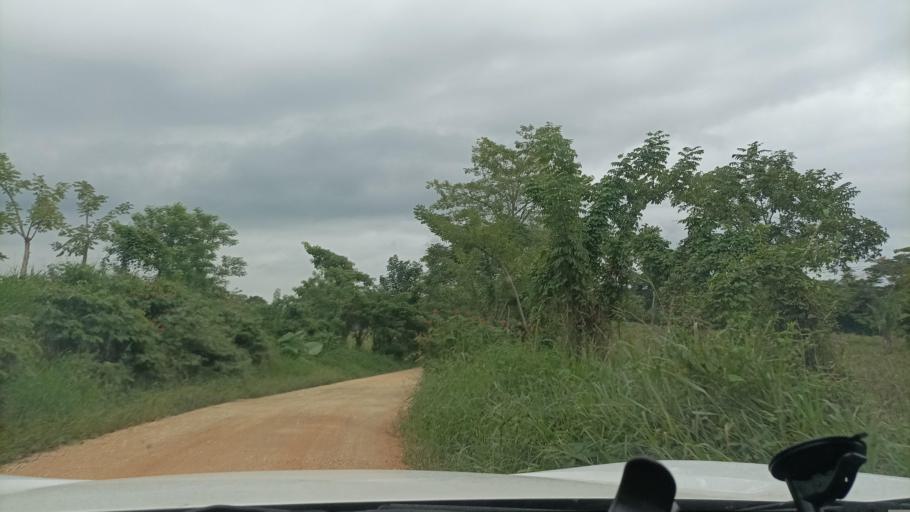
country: MX
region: Veracruz
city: Hidalgotitlan
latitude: 17.6462
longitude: -94.5076
